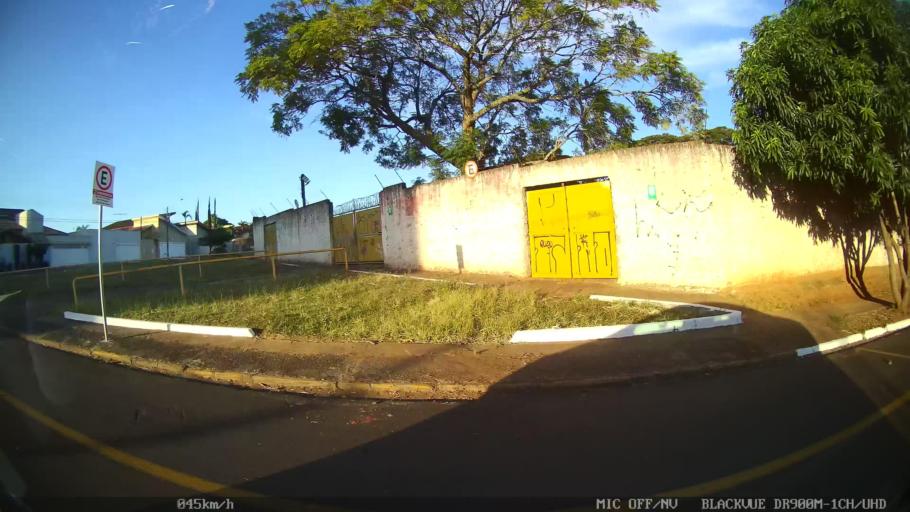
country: BR
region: Sao Paulo
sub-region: Franca
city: Franca
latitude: -20.5346
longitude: -47.3862
